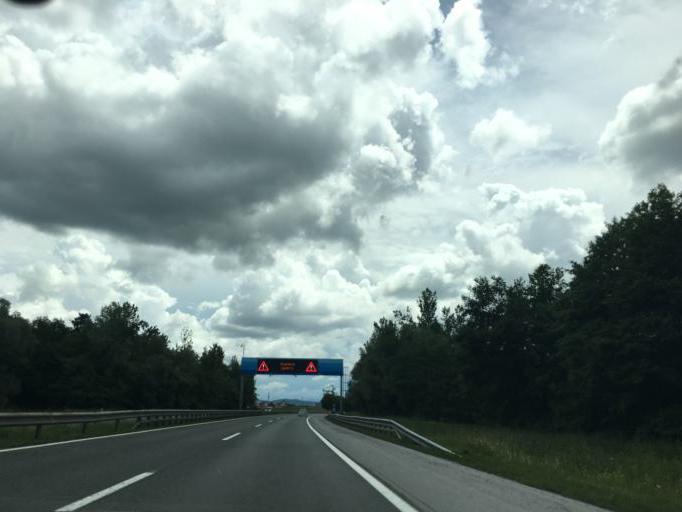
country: SI
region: Medvode
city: Zgornje Pirnice
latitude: 46.1331
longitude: 14.4806
